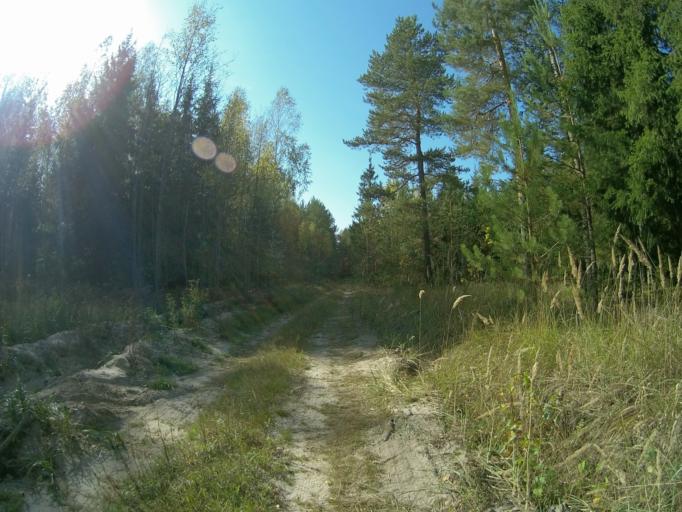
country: RU
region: Vladimir
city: Vorsha
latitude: 55.9682
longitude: 40.1293
